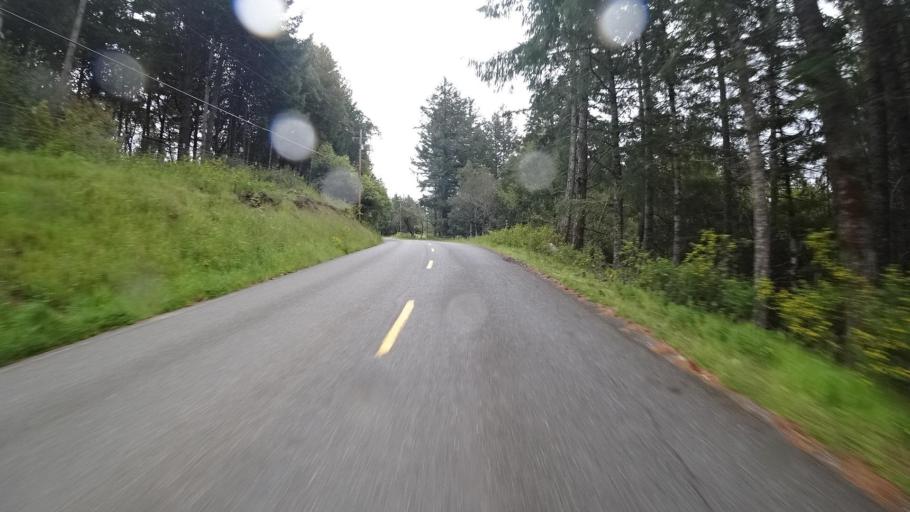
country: US
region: California
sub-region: Humboldt County
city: Redway
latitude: 40.2933
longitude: -123.8184
